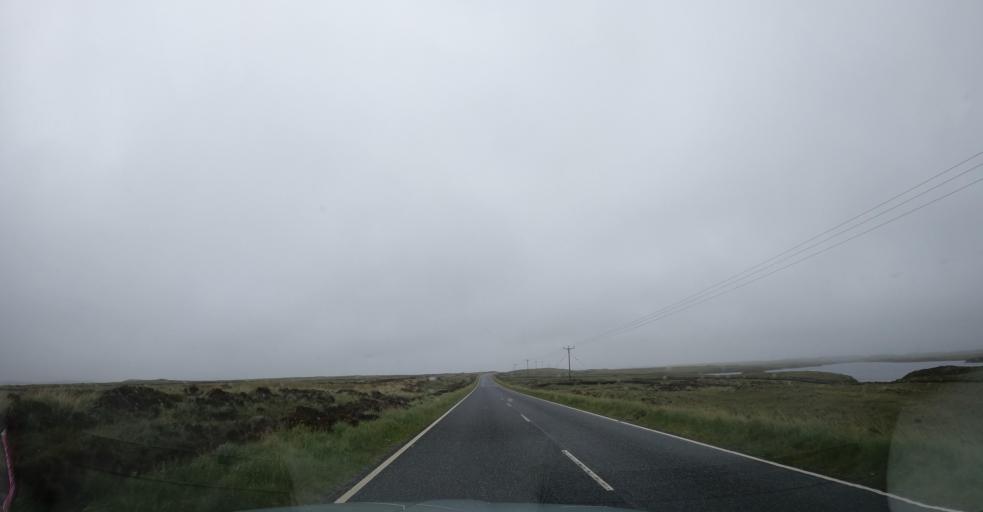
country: GB
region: Scotland
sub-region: Eilean Siar
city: Isle of North Uist
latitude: 57.5893
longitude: -7.2266
